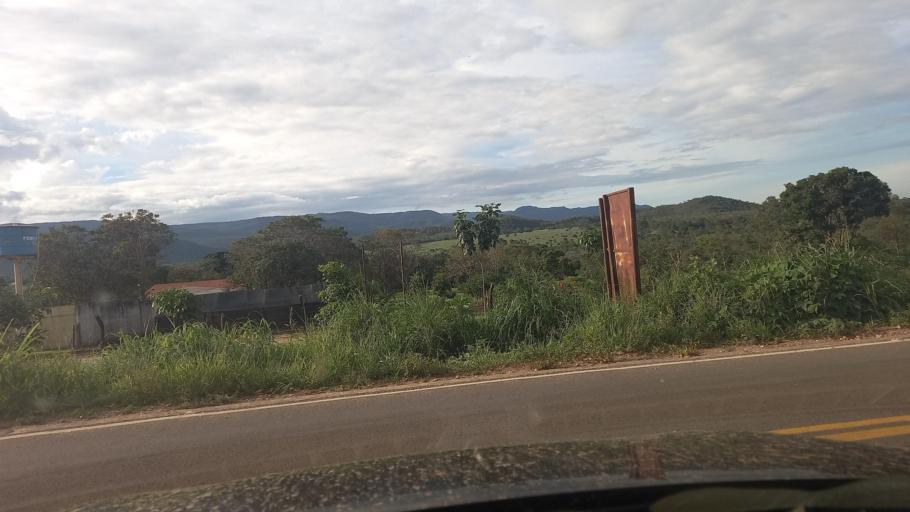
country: BR
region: Goias
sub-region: Cavalcante
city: Cavalcante
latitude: -13.7949
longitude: -47.4455
